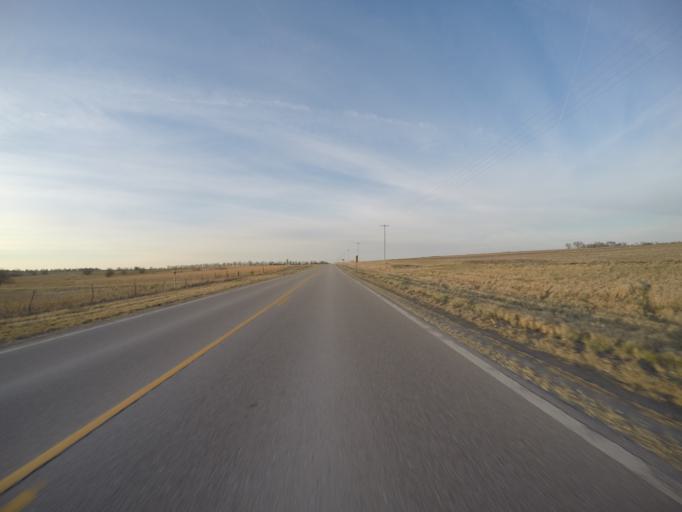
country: US
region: Kansas
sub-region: Riley County
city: Fort Riley North
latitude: 39.3547
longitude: -96.8307
